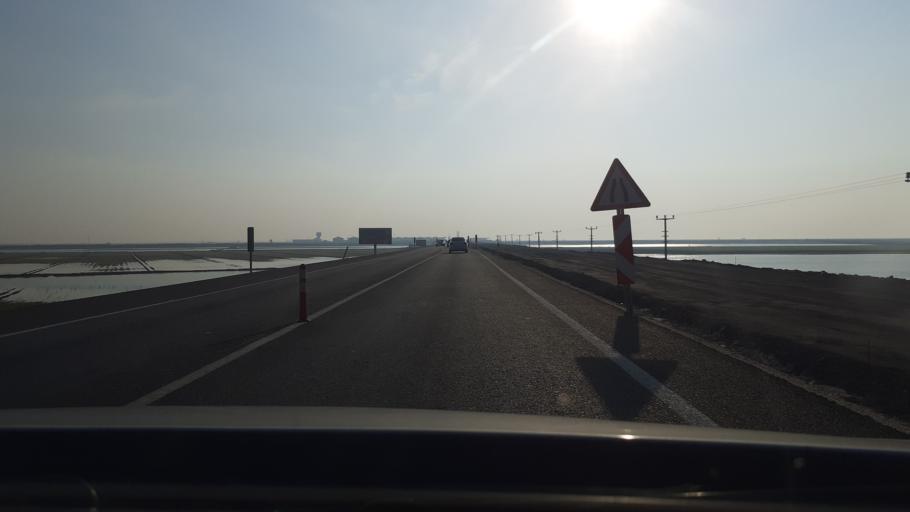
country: TR
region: Hatay
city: Serinyol
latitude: 36.3686
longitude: 36.2594
